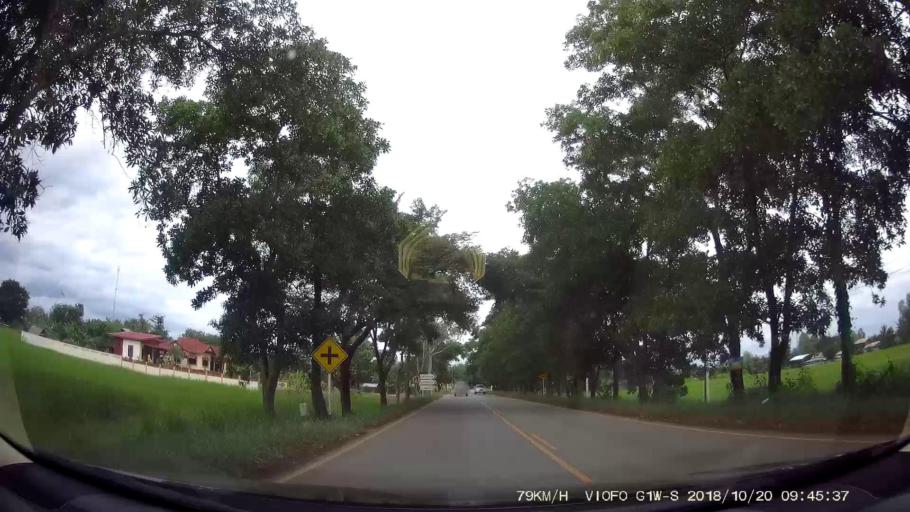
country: TH
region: Chaiyaphum
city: Khon San
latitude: 16.4911
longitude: 101.9338
